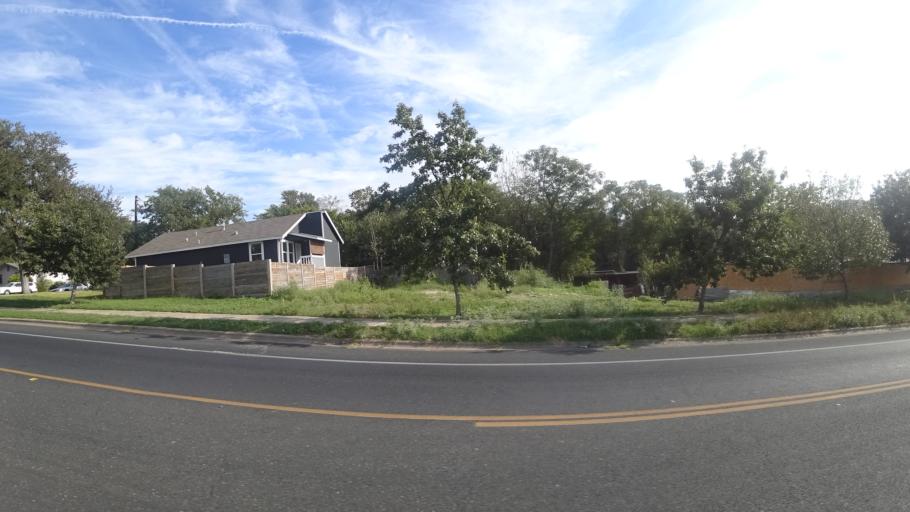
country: US
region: Texas
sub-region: Travis County
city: Austin
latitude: 30.2658
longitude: -97.7097
